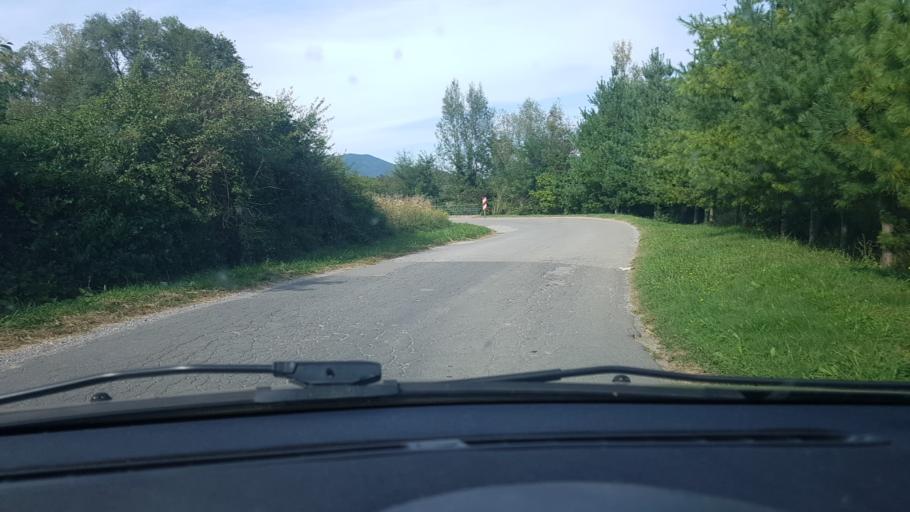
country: HR
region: Krapinsko-Zagorska
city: Zlatar
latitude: 46.1145
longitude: 16.1148
